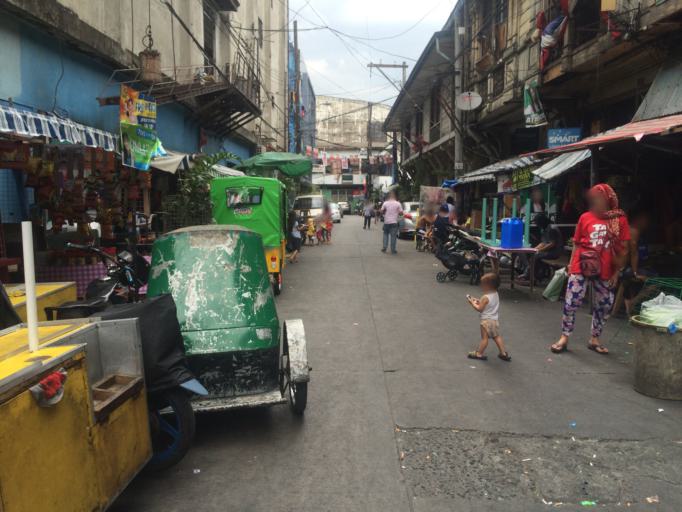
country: PH
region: Metro Manila
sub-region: City of Manila
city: Quiapo
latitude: 14.5982
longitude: 120.9845
